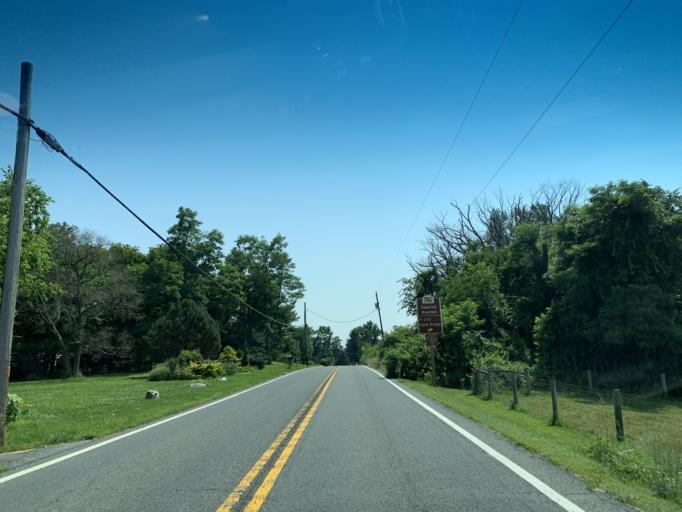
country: US
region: Maryland
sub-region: Montgomery County
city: Clarksburg
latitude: 39.2491
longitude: -77.3484
